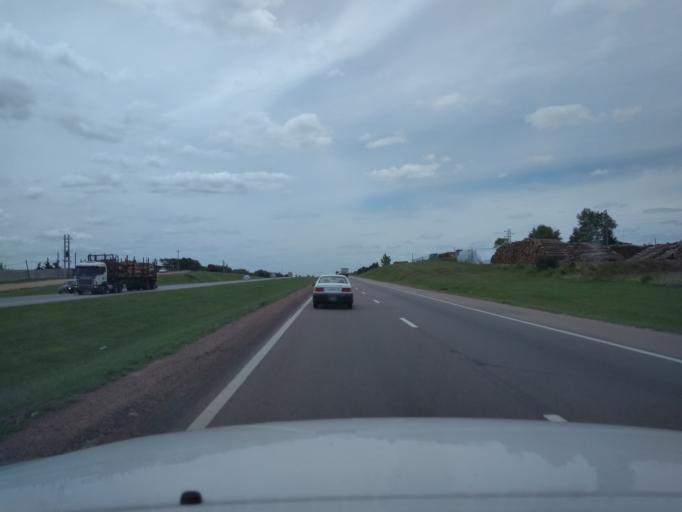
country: UY
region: Canelones
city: La Paz
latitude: -34.7445
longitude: -56.2524
